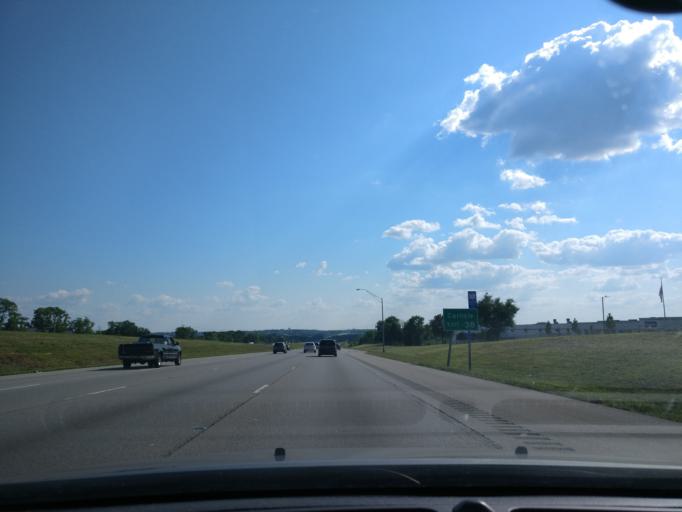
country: US
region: Ohio
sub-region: Warren County
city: Springboro
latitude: 39.5695
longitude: -84.2625
